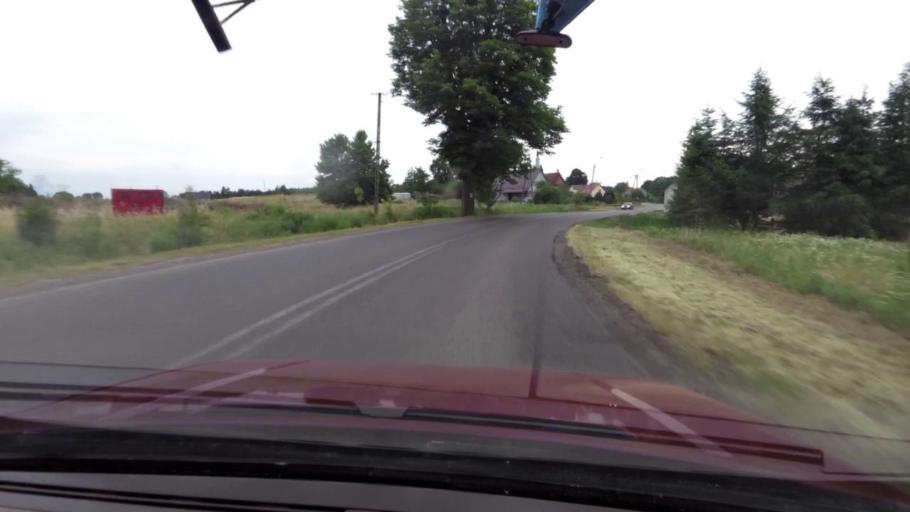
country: PL
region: West Pomeranian Voivodeship
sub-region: Powiat koszalinski
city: Sianow
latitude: 54.1780
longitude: 16.3846
